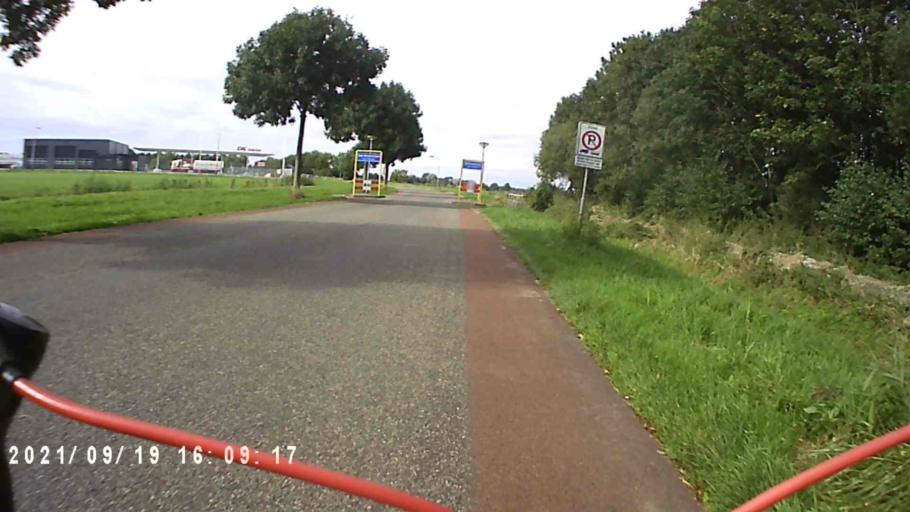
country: DE
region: Lower Saxony
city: Bunde
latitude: 53.1811
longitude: 7.2243
